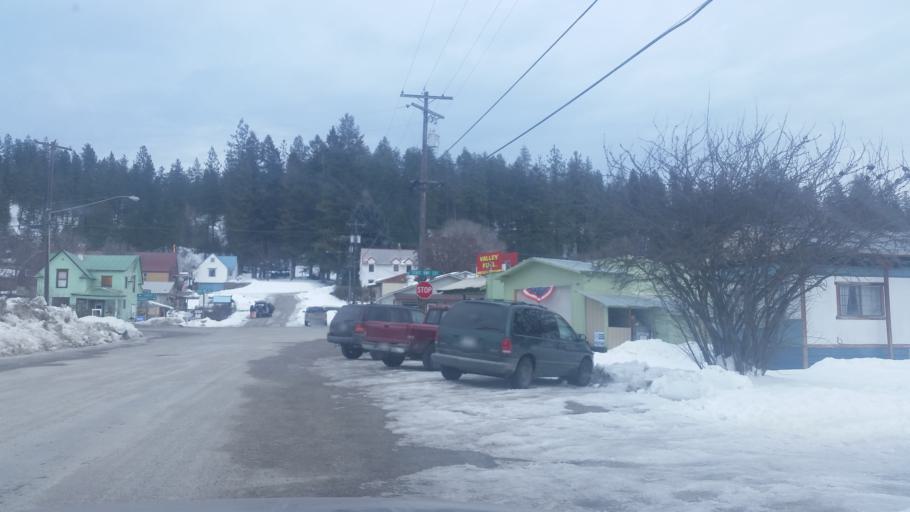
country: US
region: Washington
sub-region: Stevens County
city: Chewelah
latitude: 48.1751
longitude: -117.7256
